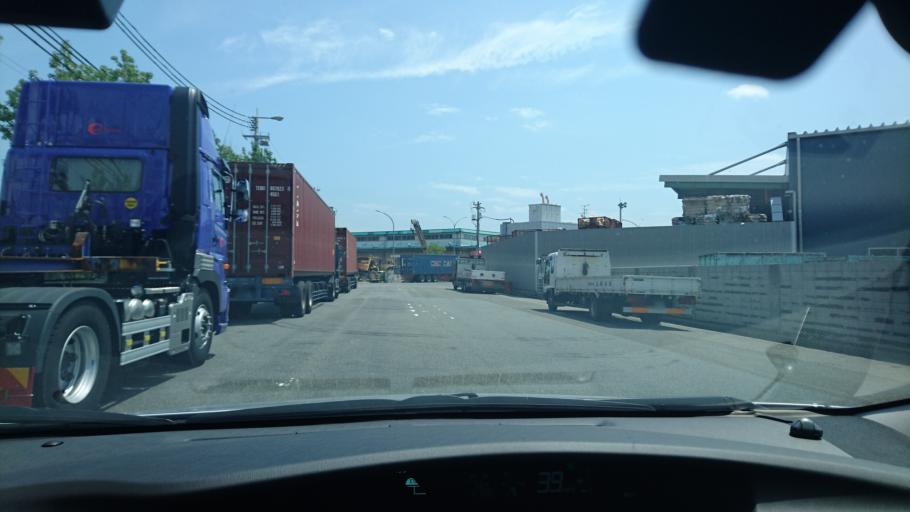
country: JP
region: Hyogo
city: Kobe
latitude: 34.6743
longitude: 135.2286
